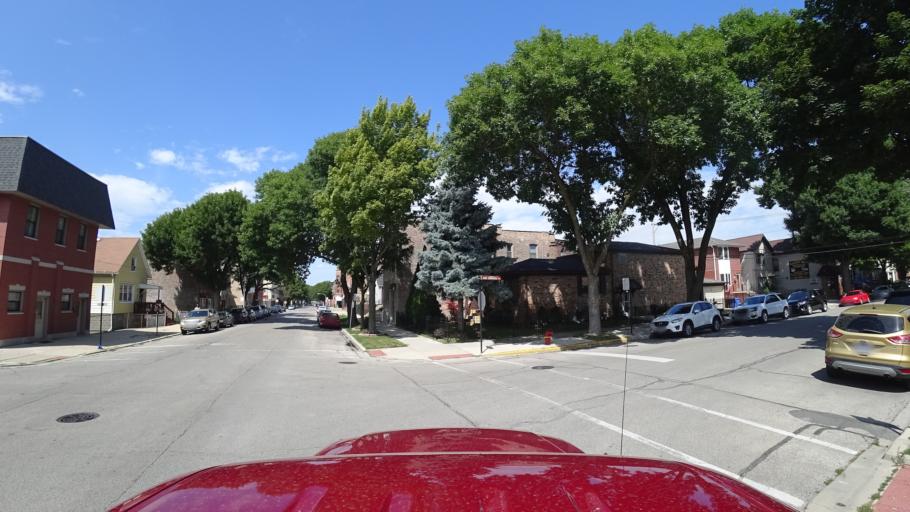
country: US
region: Illinois
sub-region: Cook County
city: Chicago
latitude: 41.8272
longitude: -87.6398
